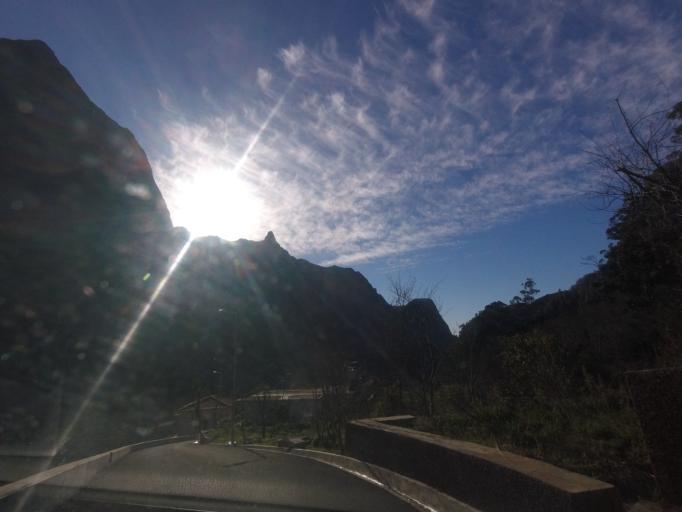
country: PT
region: Madeira
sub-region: Camara de Lobos
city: Curral das Freiras
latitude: 32.7391
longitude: -16.9708
